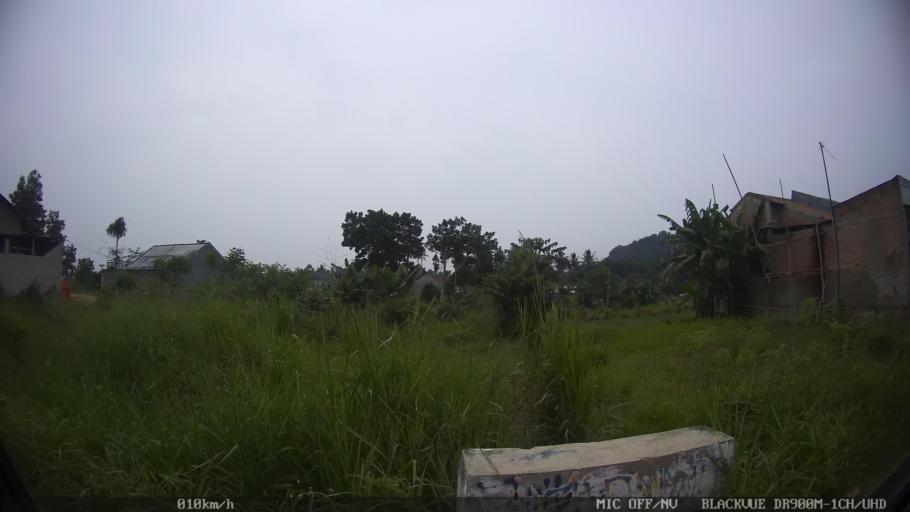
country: ID
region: Lampung
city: Panjang
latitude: -5.4225
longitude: 105.3468
